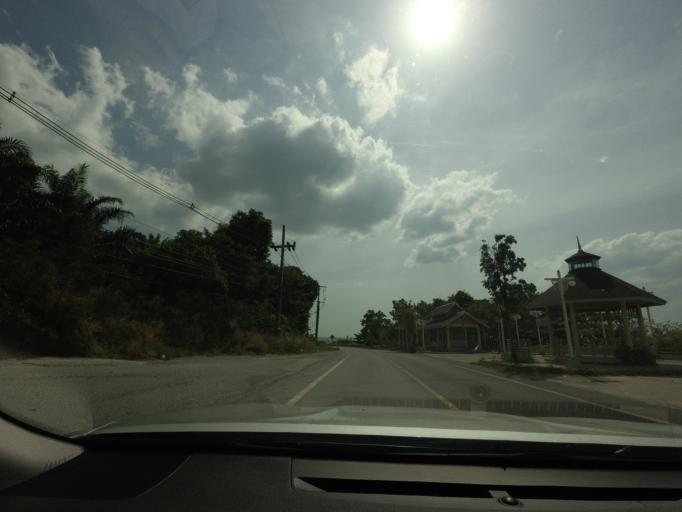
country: TH
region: Phangnga
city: Ban Ao Nang
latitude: 8.0666
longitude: 98.7440
